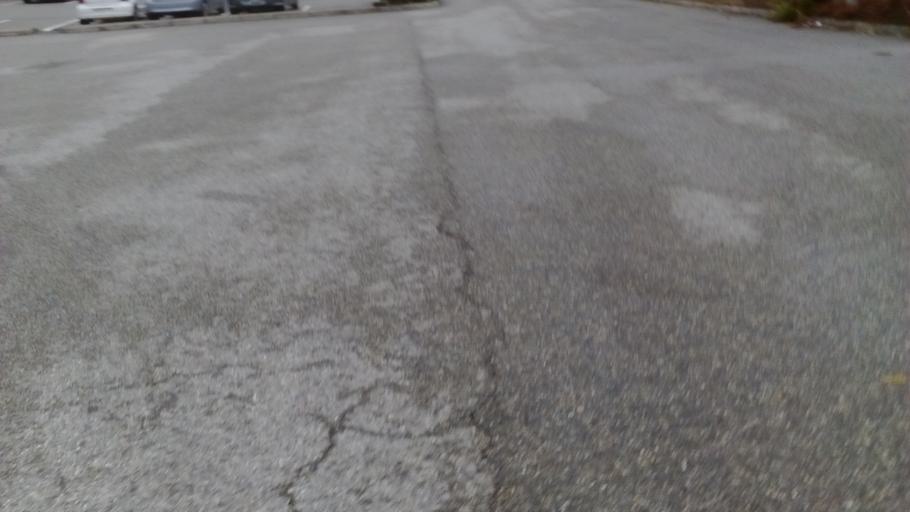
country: FR
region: Rhone-Alpes
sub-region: Departement de l'Ardeche
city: Soyons
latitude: 44.8947
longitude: 4.8607
